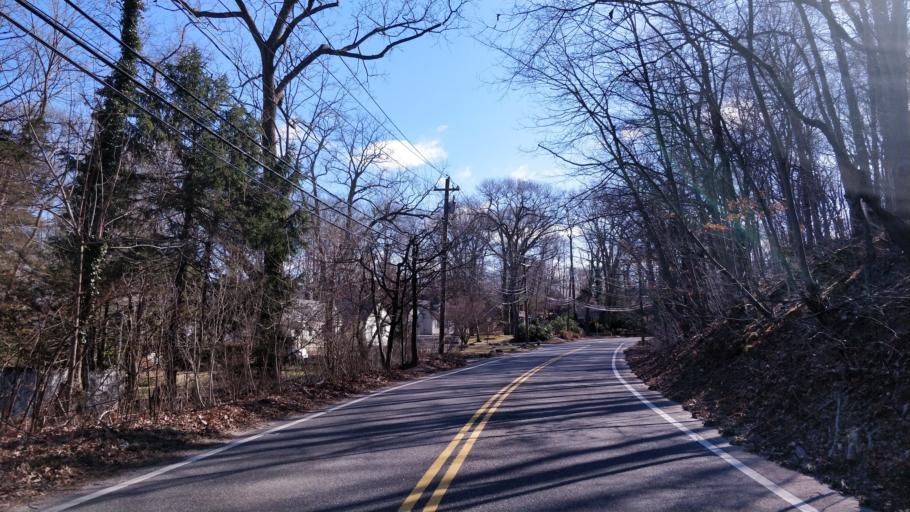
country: US
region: New York
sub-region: Suffolk County
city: Stony Brook
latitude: 40.9070
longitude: -73.1335
